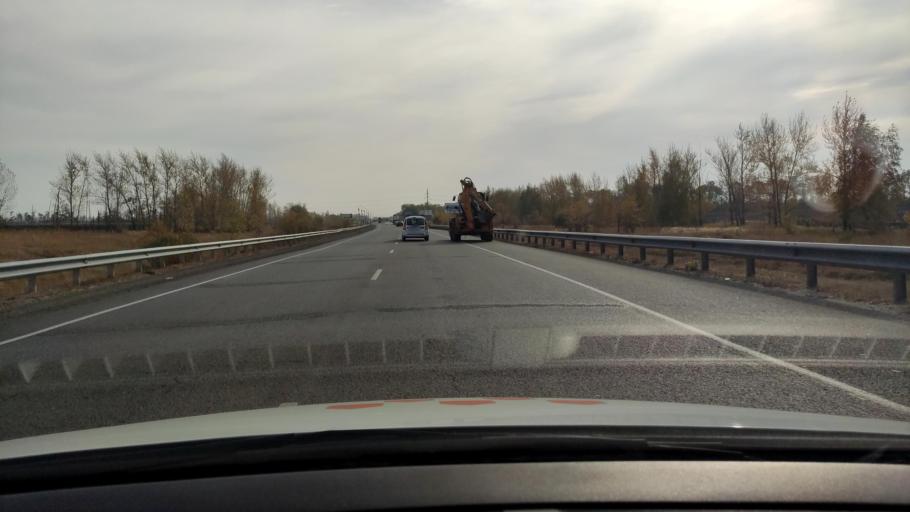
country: RU
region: Voronezj
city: Novaya Usman'
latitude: 51.6962
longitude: 39.4371
